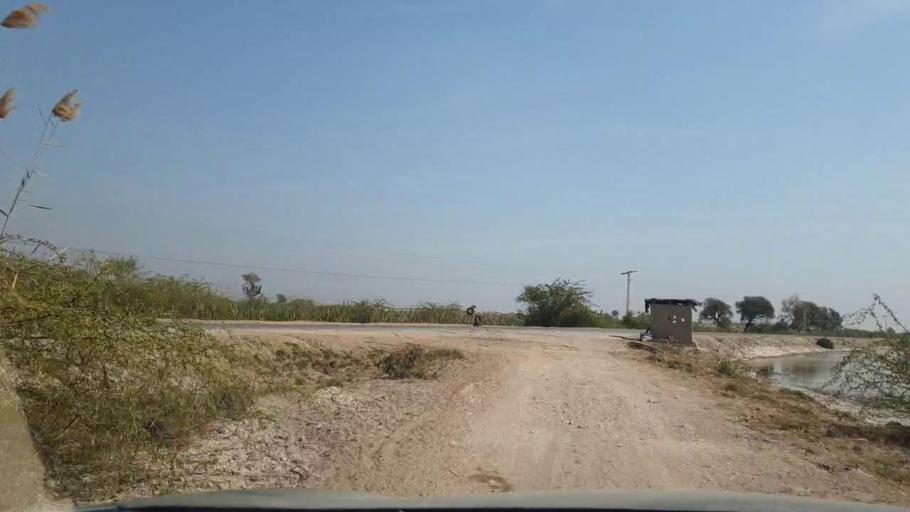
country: PK
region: Sindh
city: Berani
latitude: 25.6350
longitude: 68.8236
